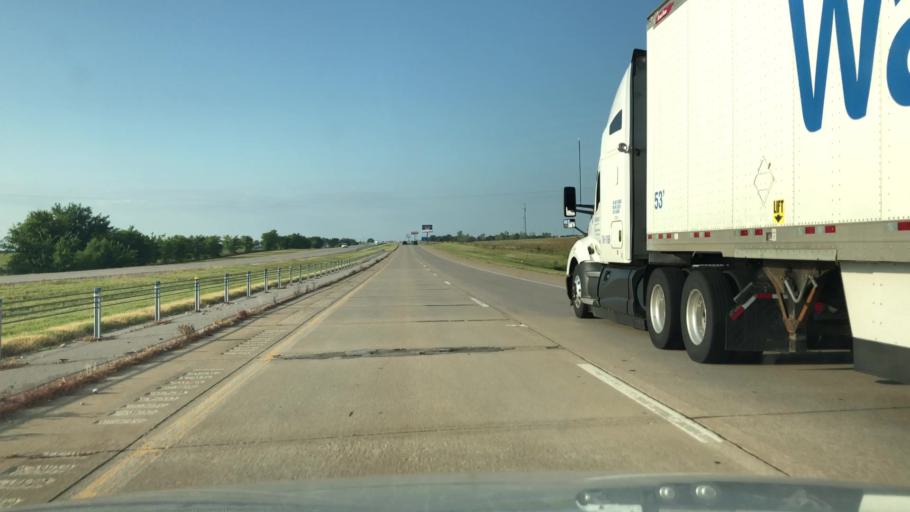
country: US
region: Oklahoma
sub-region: Osage County
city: Skiatook
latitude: 36.3781
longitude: -95.9206
